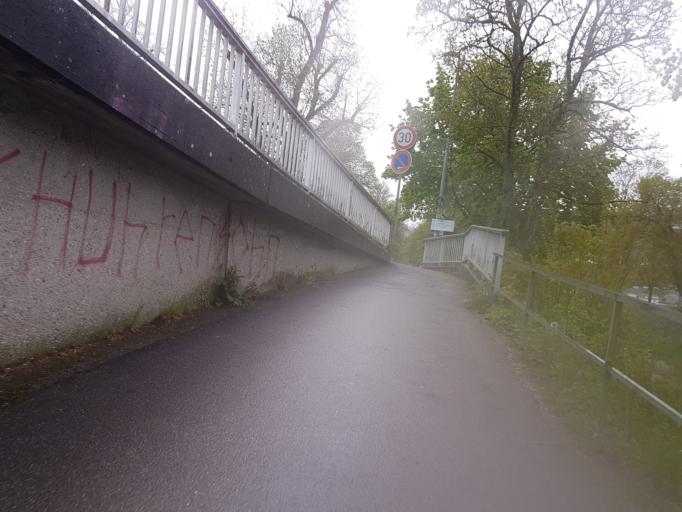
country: DE
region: Baden-Wuerttemberg
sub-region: Freiburg Region
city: Oberndorf
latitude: 48.2943
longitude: 8.5778
